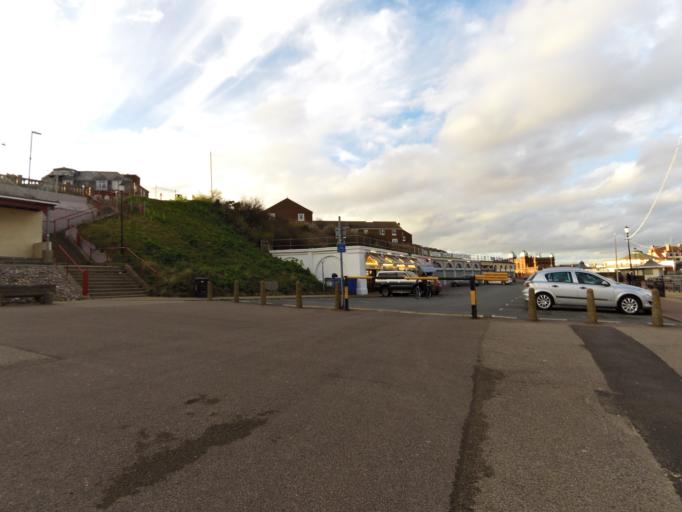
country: GB
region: England
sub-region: Norfolk
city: Gorleston-on-Sea
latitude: 52.5693
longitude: 1.7314
